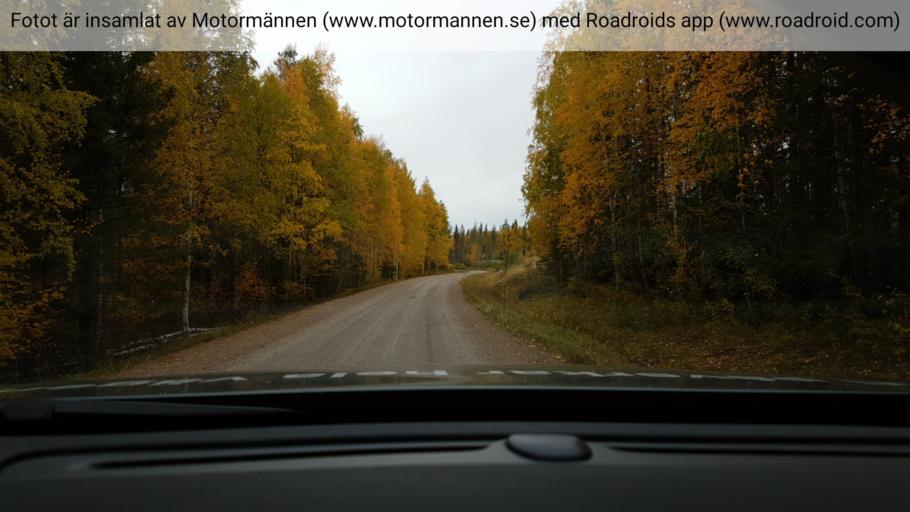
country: SE
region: Norrbotten
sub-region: Overkalix Kommun
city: OEverkalix
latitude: 66.2807
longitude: 22.9791
